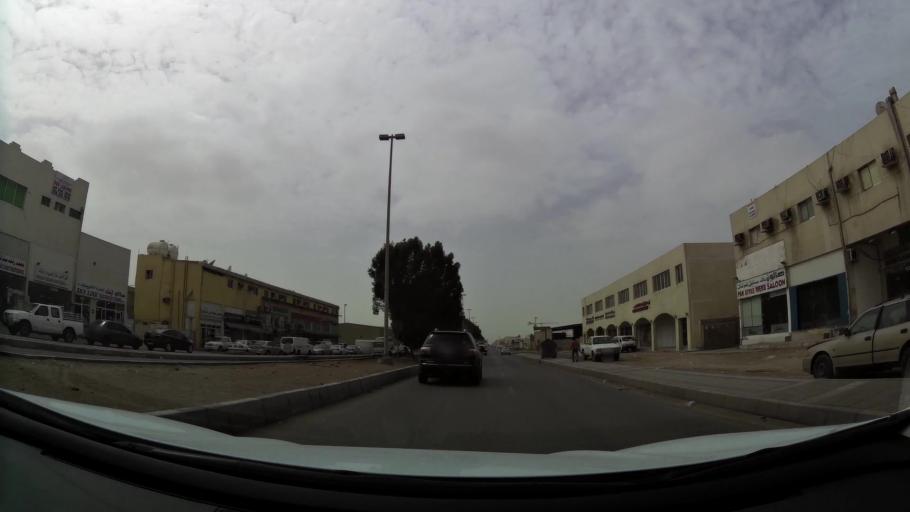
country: AE
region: Abu Dhabi
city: Abu Dhabi
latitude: 24.3548
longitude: 54.5013
